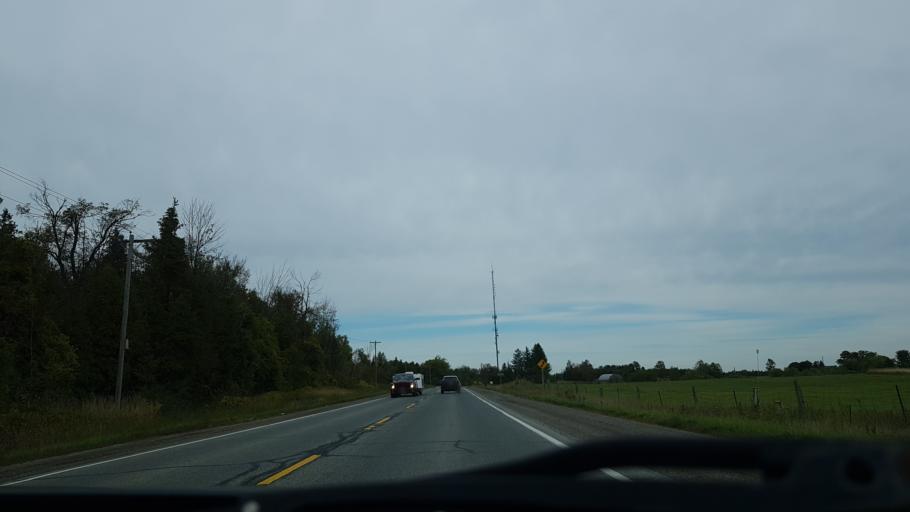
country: CA
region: Ontario
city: Orangeville
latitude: 43.9069
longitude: -79.9447
